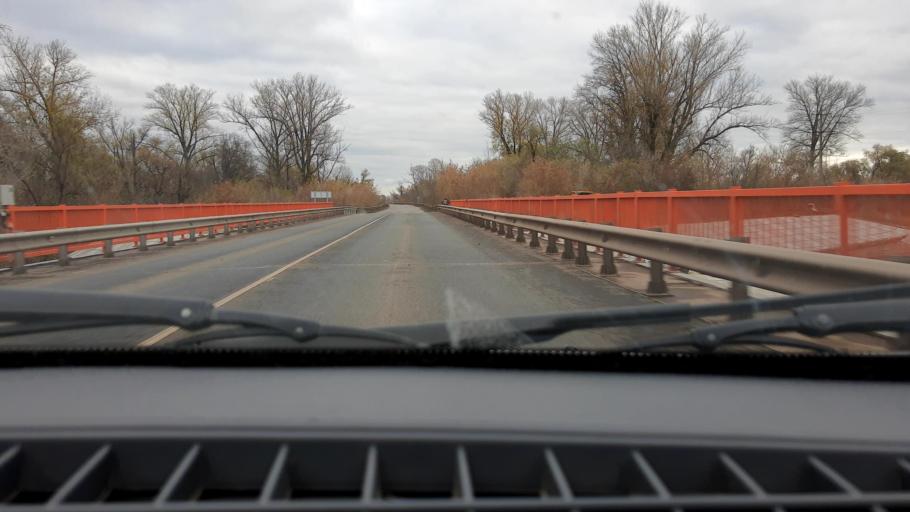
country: RU
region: Bashkortostan
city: Ufa
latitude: 54.5693
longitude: 55.9756
